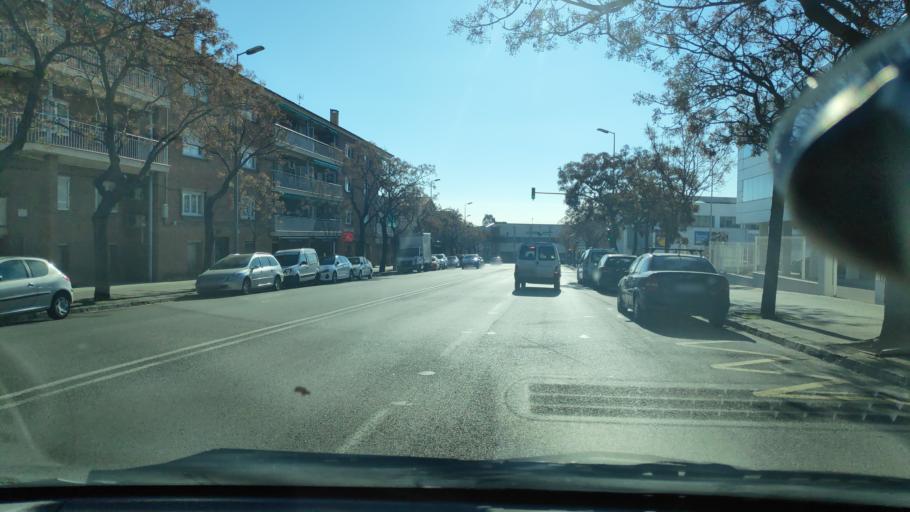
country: ES
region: Catalonia
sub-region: Provincia de Barcelona
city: Sant Quirze del Valles
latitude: 41.5430
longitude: 2.0938
